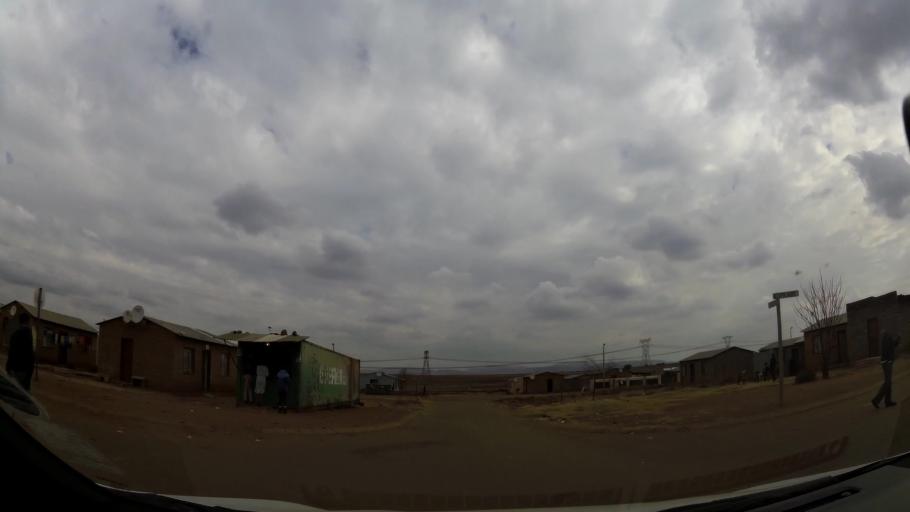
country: ZA
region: Gauteng
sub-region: Ekurhuleni Metropolitan Municipality
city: Germiston
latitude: -26.3854
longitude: 28.1168
